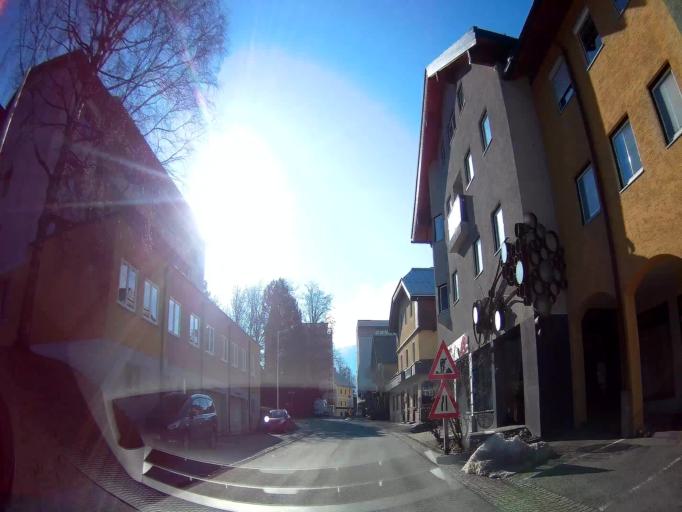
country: AT
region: Salzburg
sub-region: Politischer Bezirk Zell am See
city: Saalfelden am Steinernen Meer
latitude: 47.4286
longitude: 12.8466
